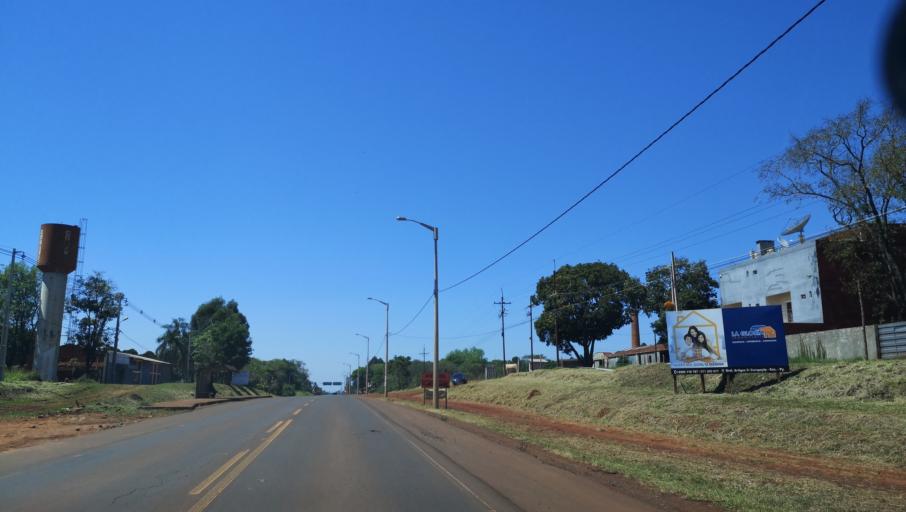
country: PY
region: Itapua
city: San Juan del Parana
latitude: -27.2780
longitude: -55.9479
